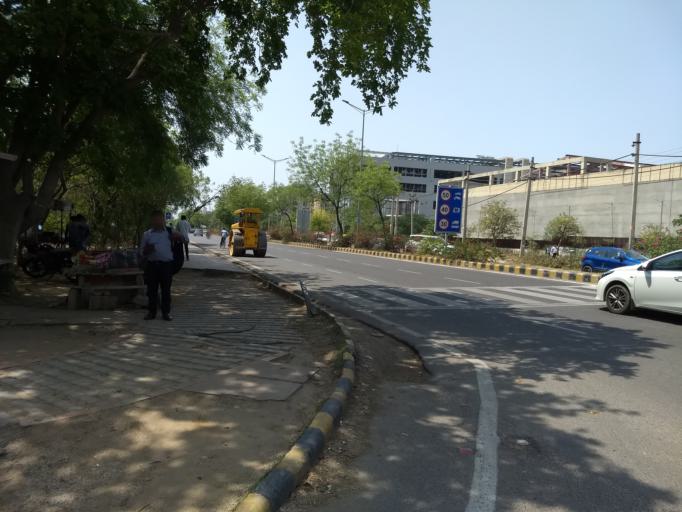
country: IN
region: Haryana
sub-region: Gurgaon
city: Gurgaon
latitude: 28.4598
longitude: 77.0691
